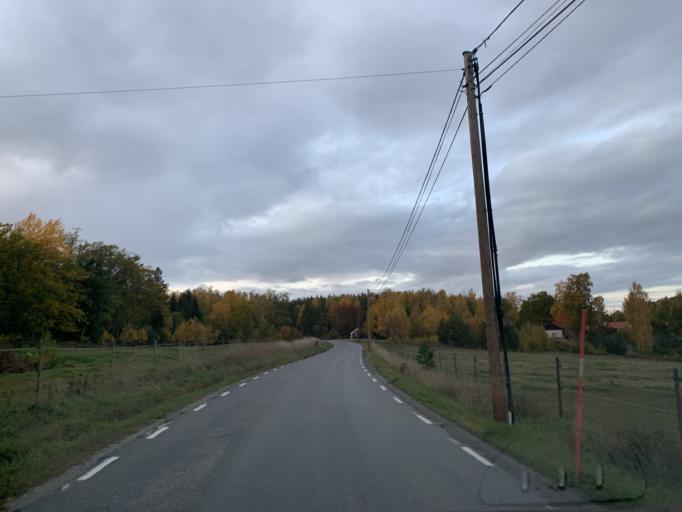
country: SE
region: Stockholm
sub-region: Nynashamns Kommun
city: Osmo
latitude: 58.9155
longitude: 17.7806
